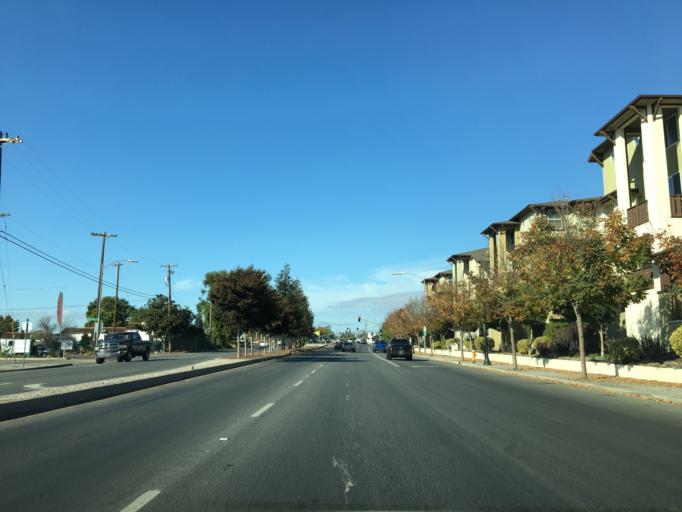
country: US
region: California
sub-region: Santa Clara County
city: San Jose
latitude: 37.3609
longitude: -121.8911
